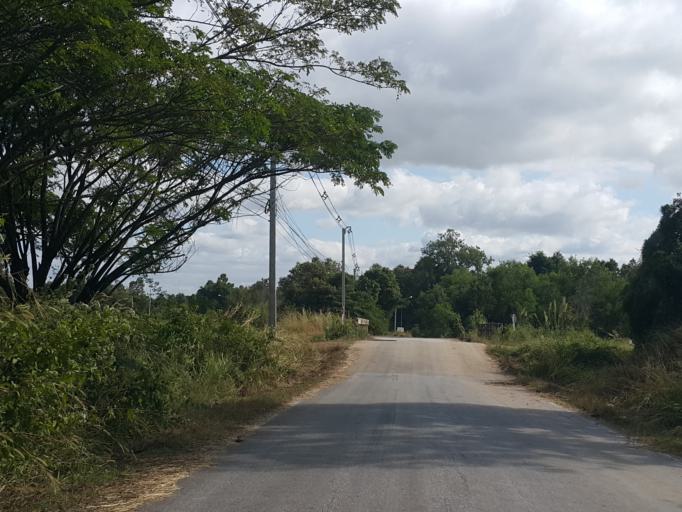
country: TH
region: Lampang
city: Hang Chat
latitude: 18.3289
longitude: 99.3888
